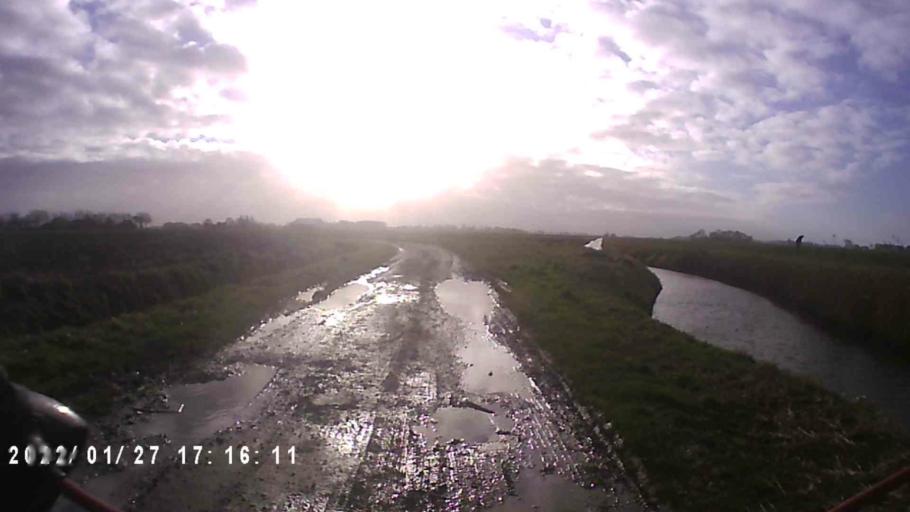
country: NL
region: Friesland
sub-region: Gemeente Dongeradeel
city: Anjum
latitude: 53.3918
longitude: 6.0985
